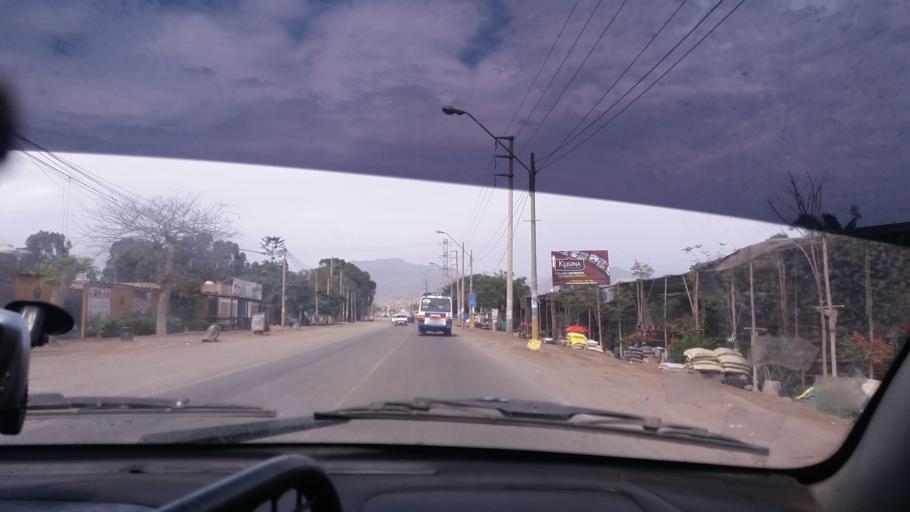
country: PE
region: Lima
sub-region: Lima
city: Punta Hermosa
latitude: -12.2543
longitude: -76.8778
